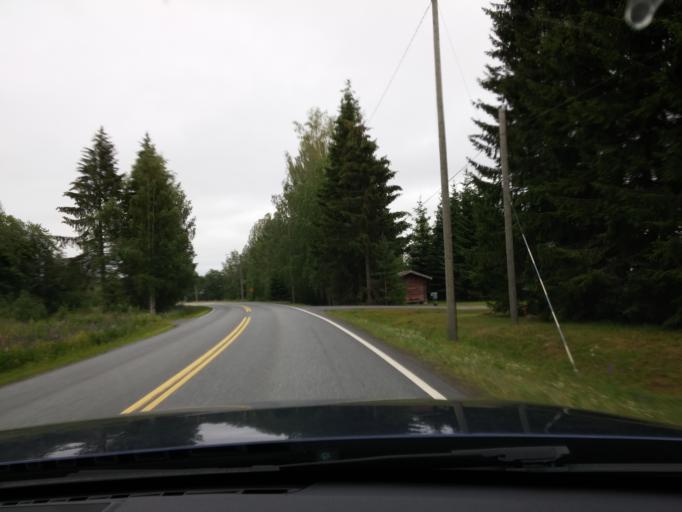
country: FI
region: Central Finland
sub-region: Joutsa
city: Joutsa
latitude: 61.8126
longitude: 25.9379
